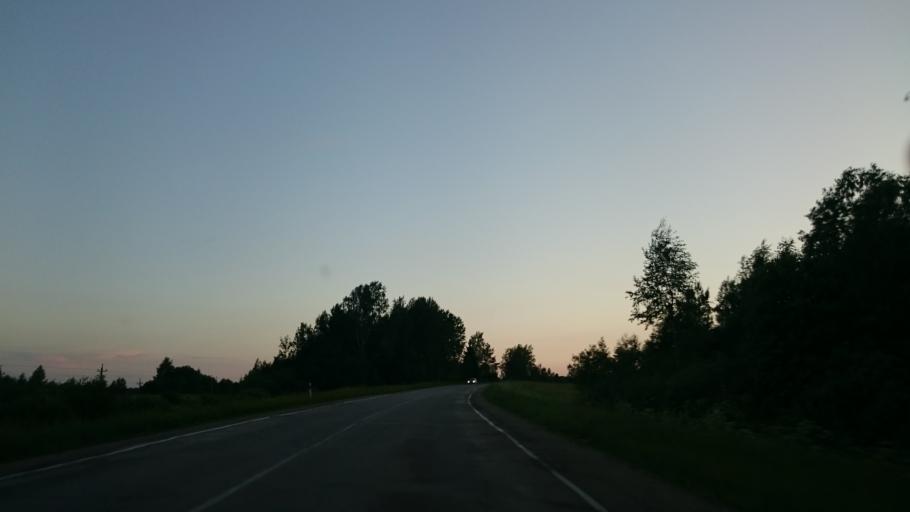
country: LV
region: Ludzas Rajons
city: Ludza
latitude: 56.5345
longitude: 27.6094
